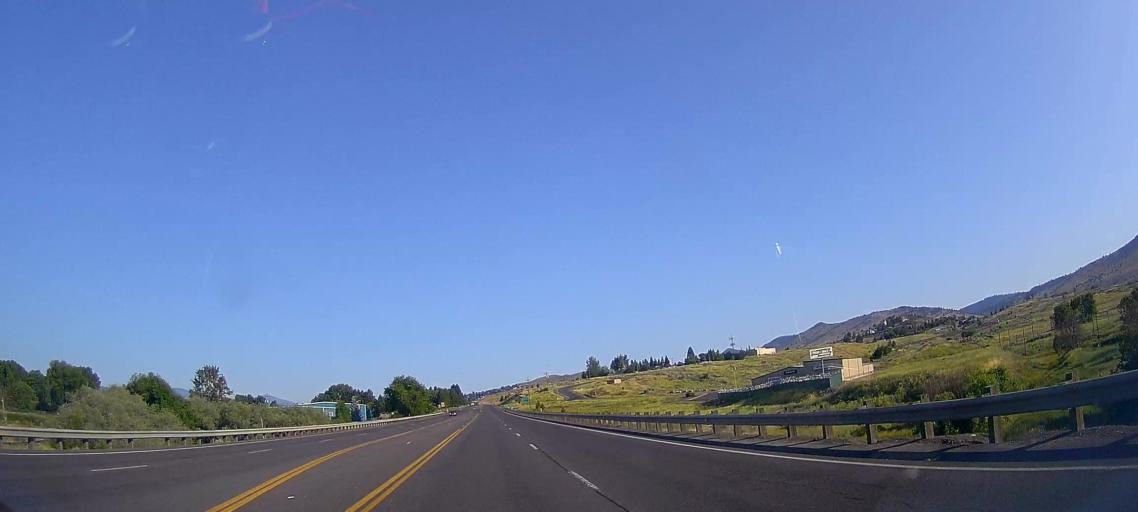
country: US
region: Oregon
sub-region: Klamath County
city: Altamont
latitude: 42.2153
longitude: -121.7450
